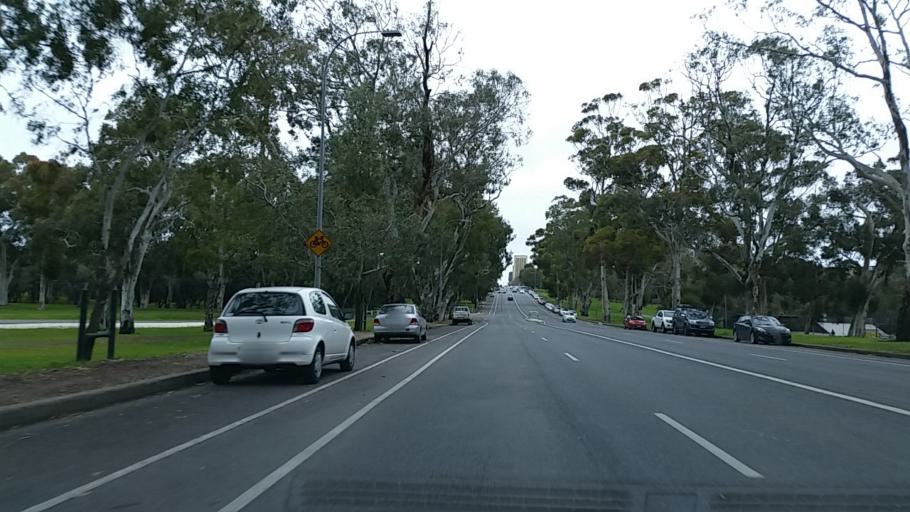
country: AU
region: South Australia
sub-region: Adelaide
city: Adelaide
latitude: -34.9277
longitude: 138.6189
